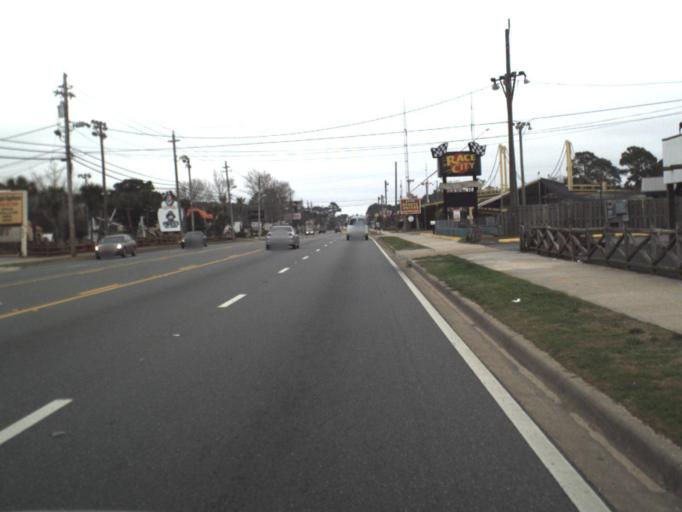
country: US
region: Florida
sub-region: Bay County
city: Panama City Beach
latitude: 30.1796
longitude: -85.7955
